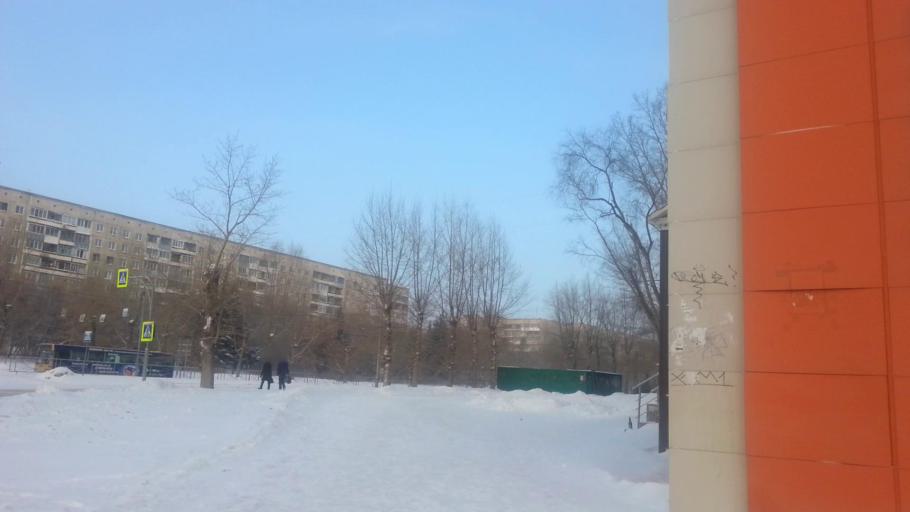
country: RU
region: Altai Krai
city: Novosilikatnyy
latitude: 53.3622
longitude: 83.6762
